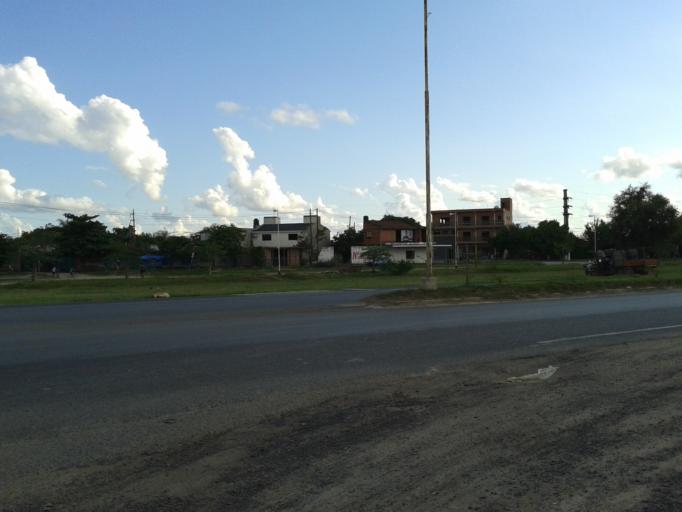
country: AR
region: Formosa
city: Clorinda
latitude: -25.2903
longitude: -57.7297
